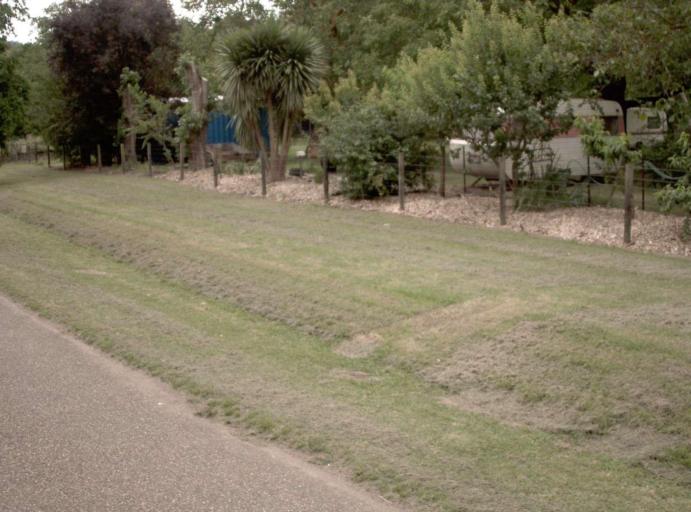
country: AU
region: Victoria
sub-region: East Gippsland
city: Bairnsdale
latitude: -37.4660
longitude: 147.2515
